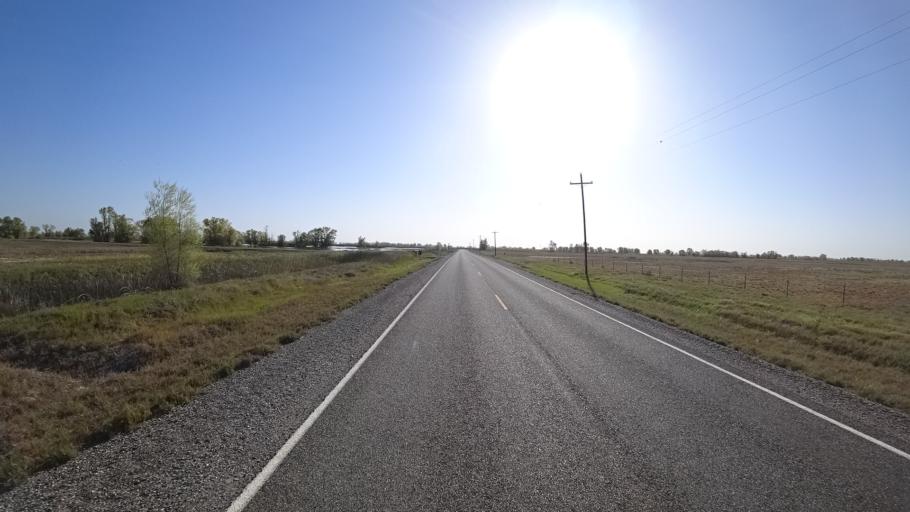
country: US
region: California
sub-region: Glenn County
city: Willows
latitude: 39.4076
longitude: -122.1425
